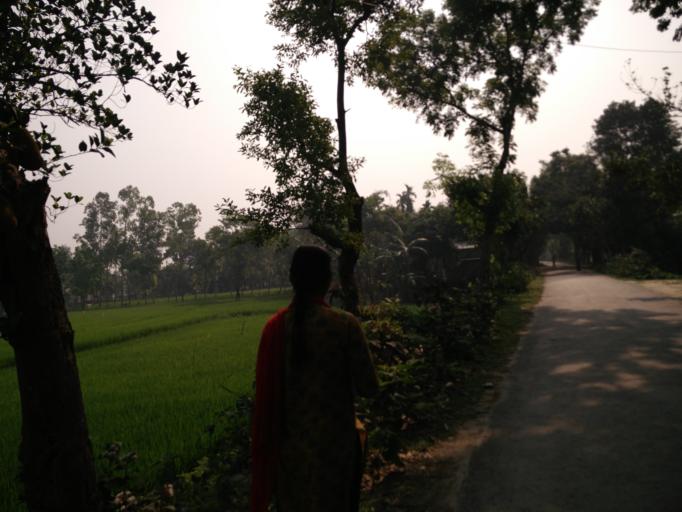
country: BD
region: Dhaka
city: Muktagacha
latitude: 24.9098
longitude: 90.1607
